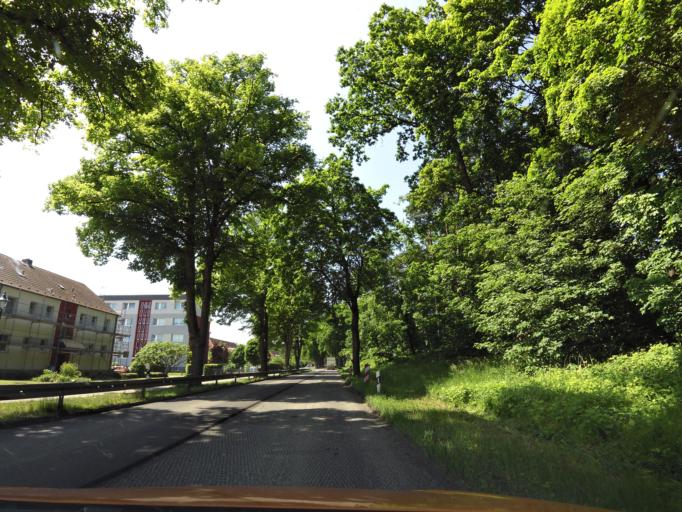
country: DE
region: Mecklenburg-Vorpommern
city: Selmsdorf
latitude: 53.8839
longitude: 10.8435
